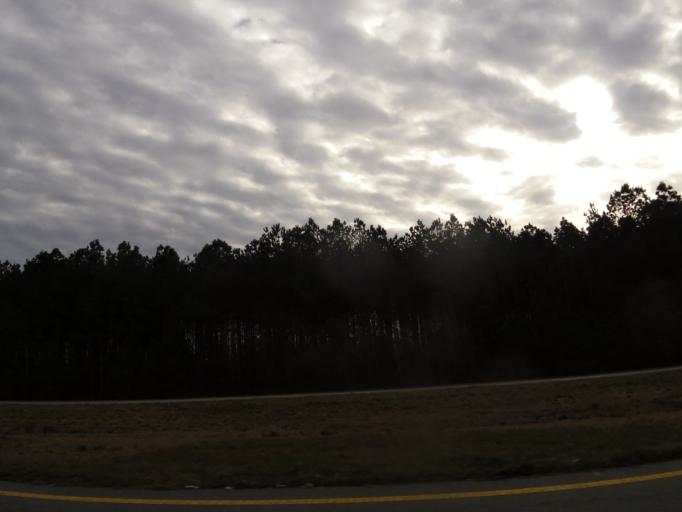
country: US
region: North Carolina
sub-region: Hertford County
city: Murfreesboro
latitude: 36.4262
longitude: -77.1127
